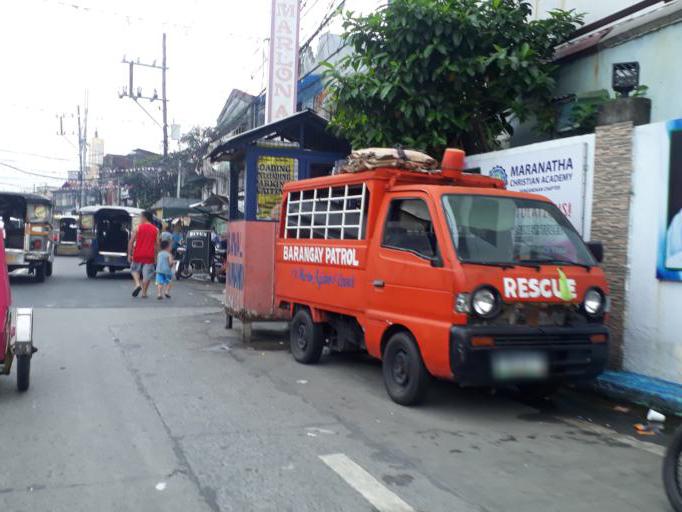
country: PH
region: Metro Manila
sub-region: Caloocan City
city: Niugan
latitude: 14.6605
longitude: 120.9705
